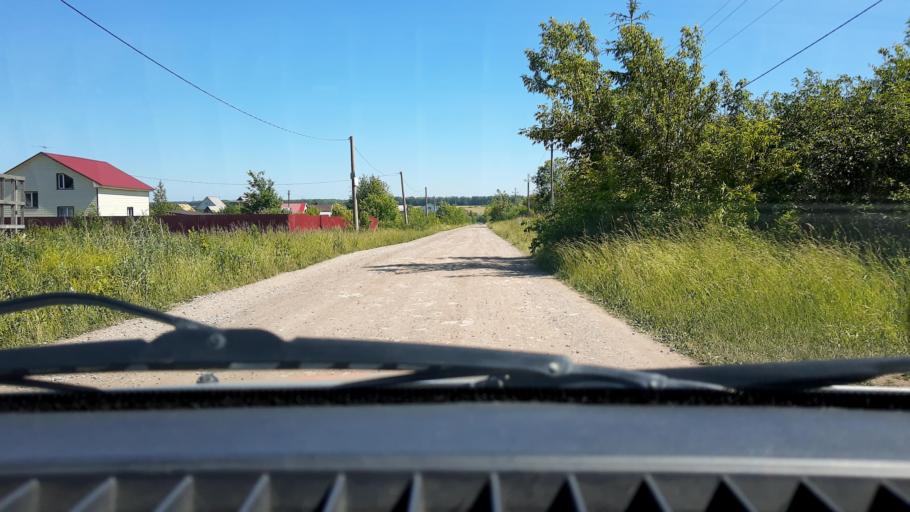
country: RU
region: Bashkortostan
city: Avdon
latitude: 54.5460
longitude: 55.7191
